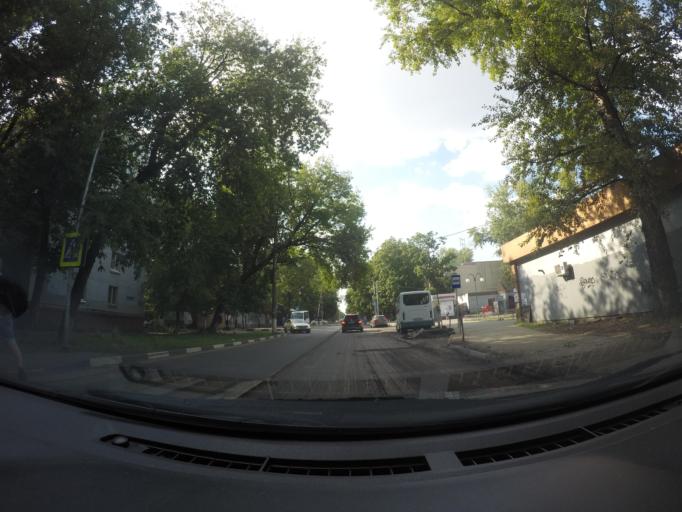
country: RU
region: Moskovskaya
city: Tomilino
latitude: 55.6677
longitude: 37.9232
